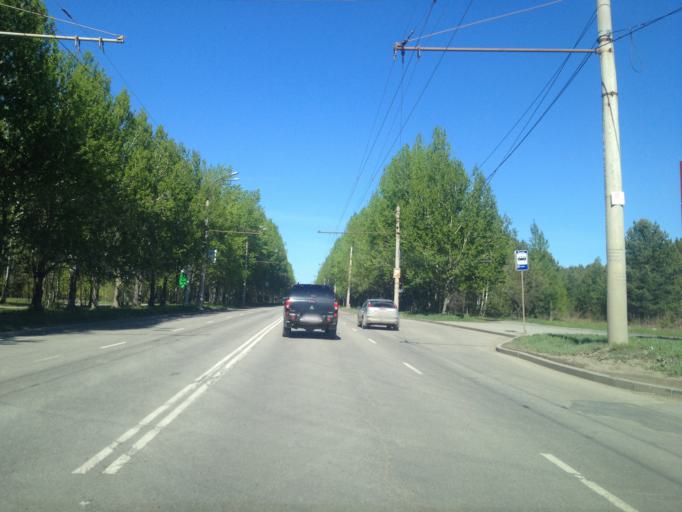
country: RU
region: Sverdlovsk
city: Sovkhoznyy
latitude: 56.7730
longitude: 60.5461
